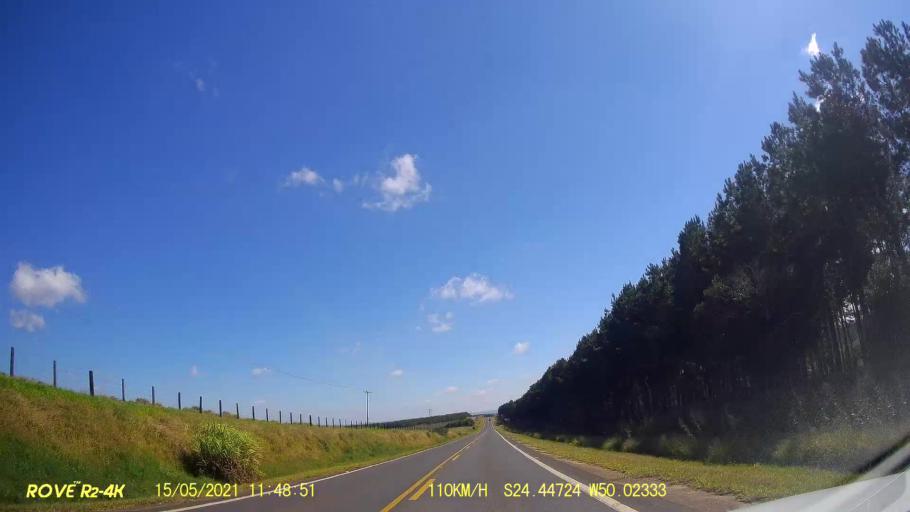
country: BR
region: Parana
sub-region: Pirai Do Sul
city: Pirai do Sul
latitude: -24.4477
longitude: -50.0233
